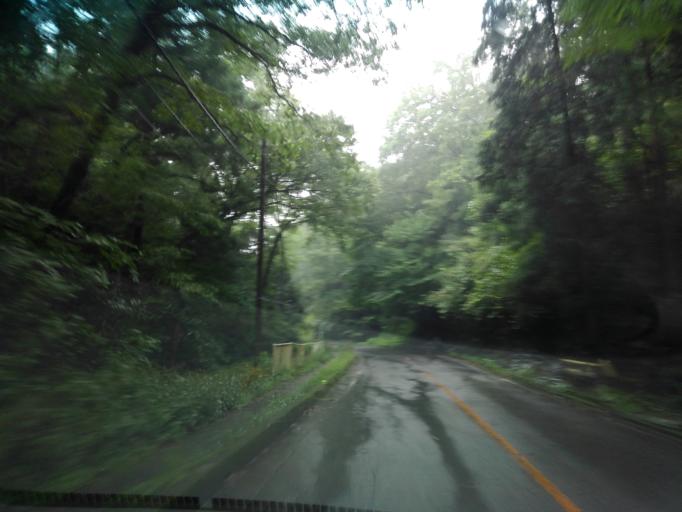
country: JP
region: Saitama
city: Hanno
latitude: 35.8227
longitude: 139.3422
